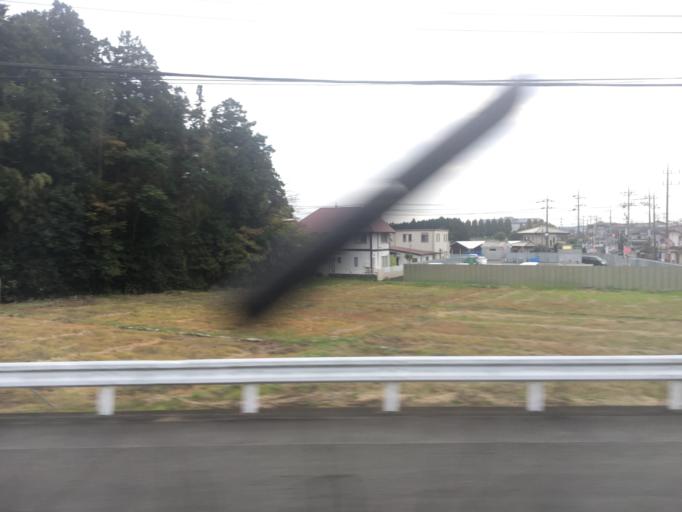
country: JP
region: Saitama
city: Hanno
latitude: 35.8648
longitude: 139.3326
